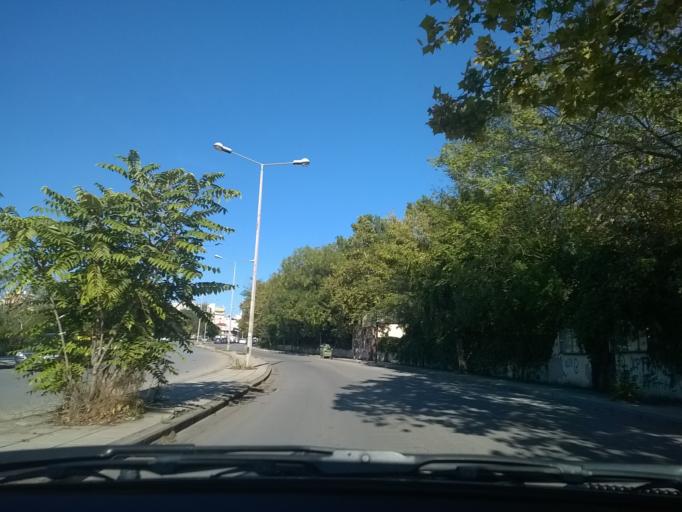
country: GR
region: Central Macedonia
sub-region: Nomos Thessalonikis
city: Stavroupoli
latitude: 40.6571
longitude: 22.9399
